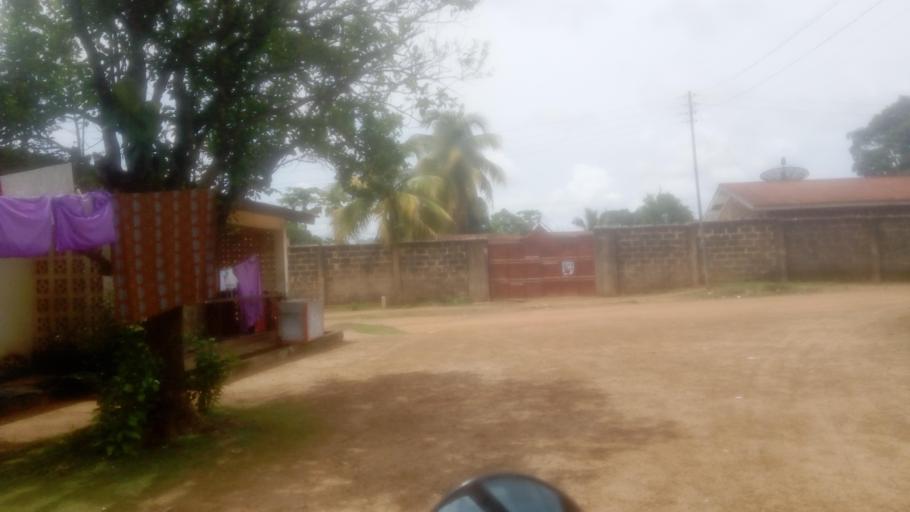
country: SL
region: Southern Province
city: Bo
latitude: 7.9515
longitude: -11.7166
